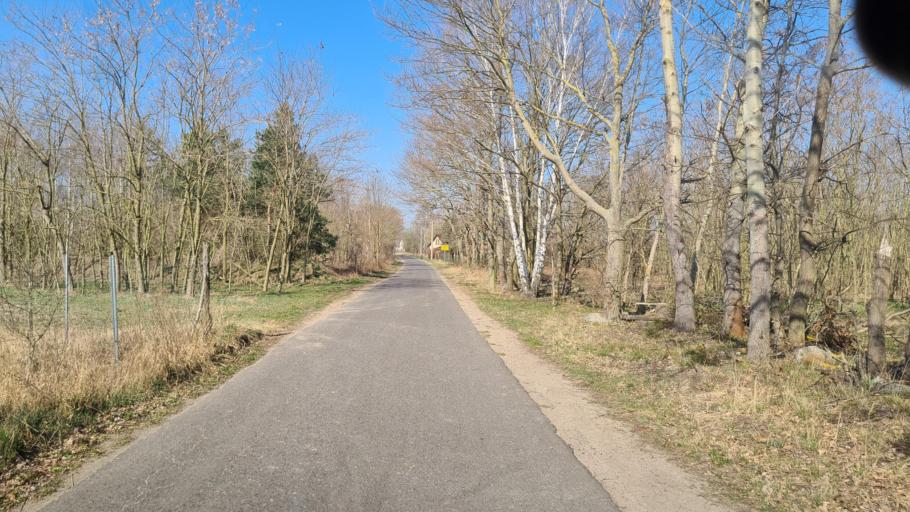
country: DE
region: Brandenburg
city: Calau
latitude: 51.7972
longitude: 13.9808
